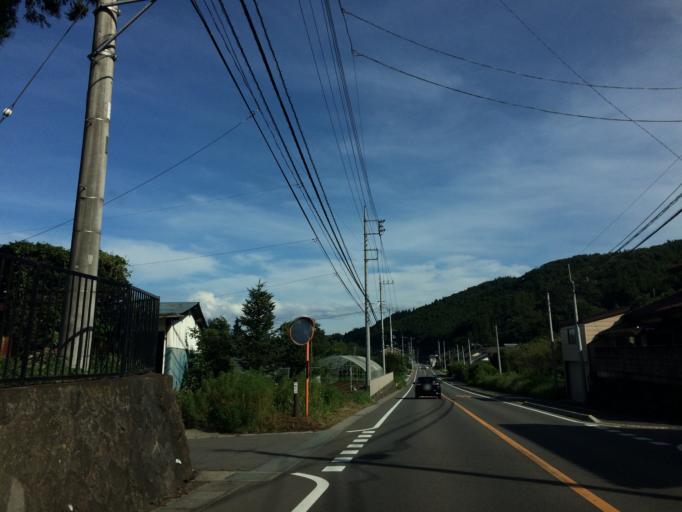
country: JP
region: Gunma
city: Nakanojomachi
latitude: 36.5526
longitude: 138.9036
